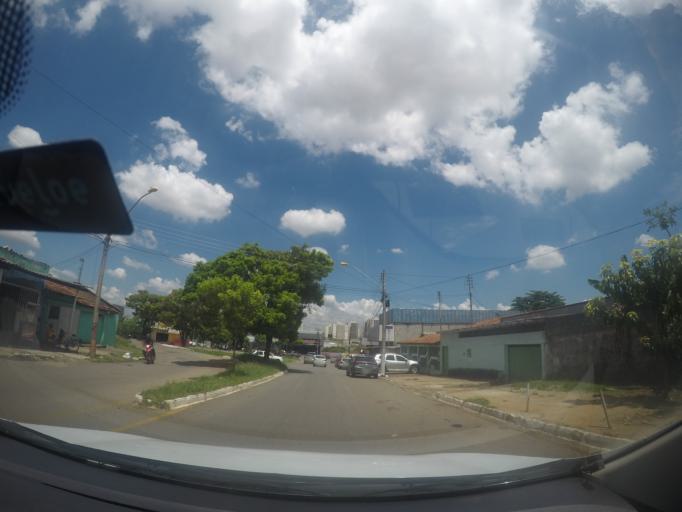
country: BR
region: Goias
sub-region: Goiania
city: Goiania
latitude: -16.6894
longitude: -49.3192
